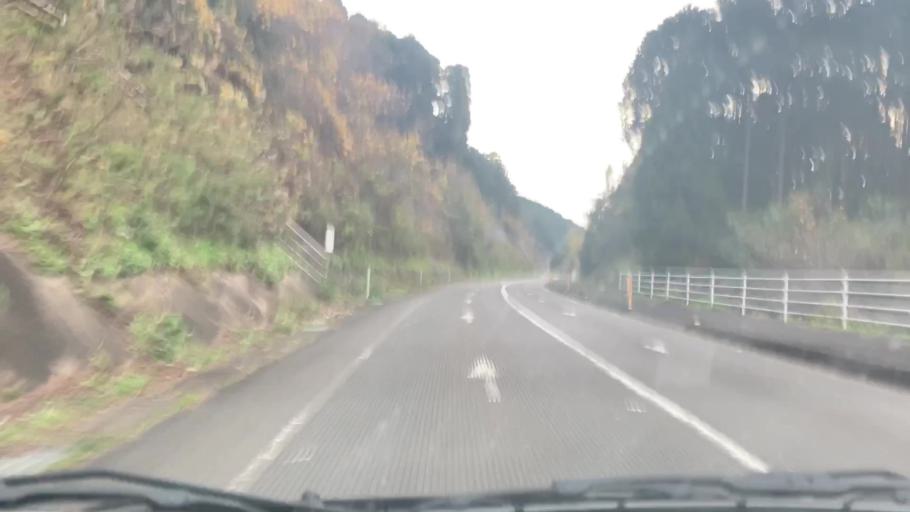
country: JP
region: Saga Prefecture
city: Kashima
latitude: 33.0465
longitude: 130.0717
